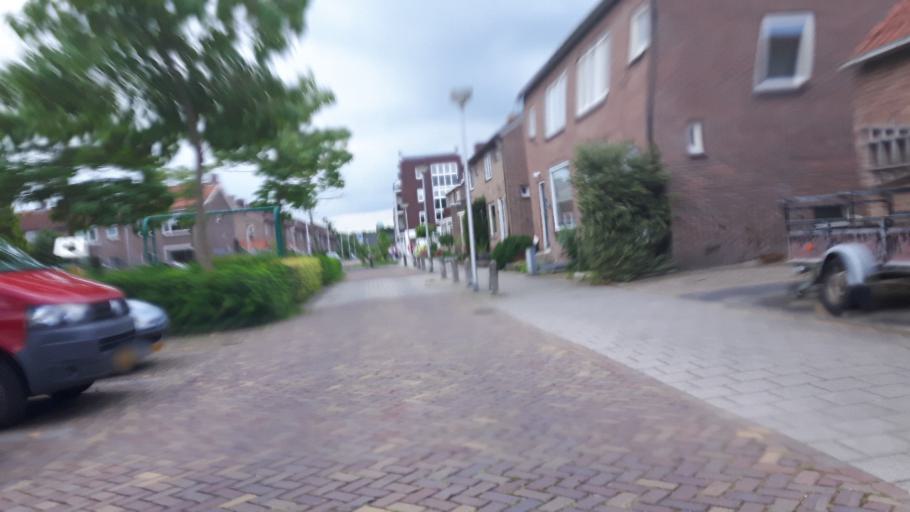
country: NL
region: South Holland
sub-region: Molenwaard
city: Liesveld
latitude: 51.9353
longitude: 4.7843
